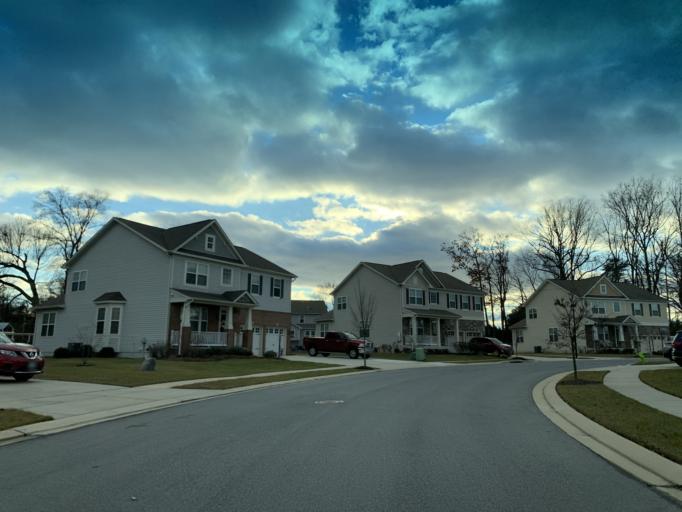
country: US
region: Maryland
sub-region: Baltimore County
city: Middle River
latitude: 39.3440
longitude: -76.4318
